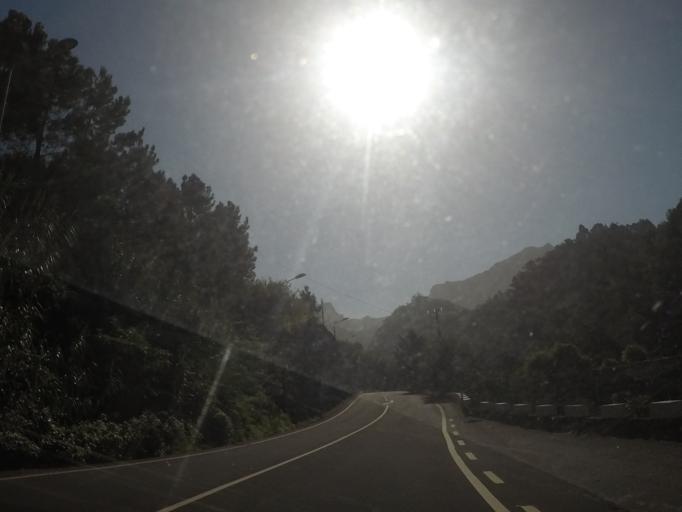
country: PT
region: Madeira
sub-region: Sao Vicente
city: Sao Vicente
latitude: 32.7888
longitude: -17.0302
